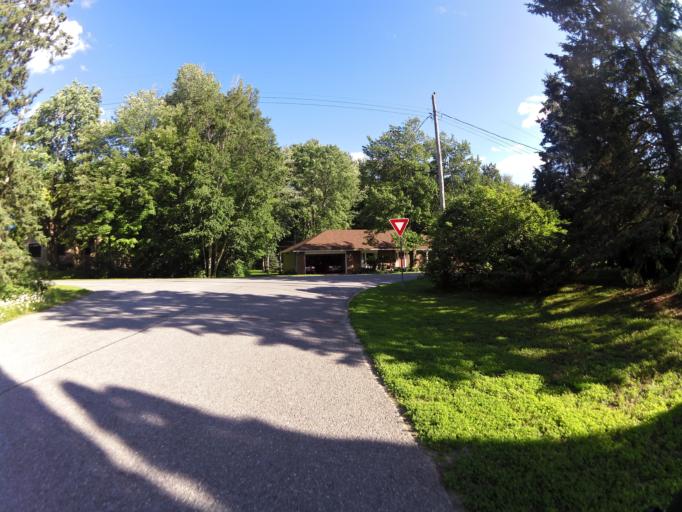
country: CA
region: Ontario
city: Bells Corners
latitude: 45.3229
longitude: -75.7351
